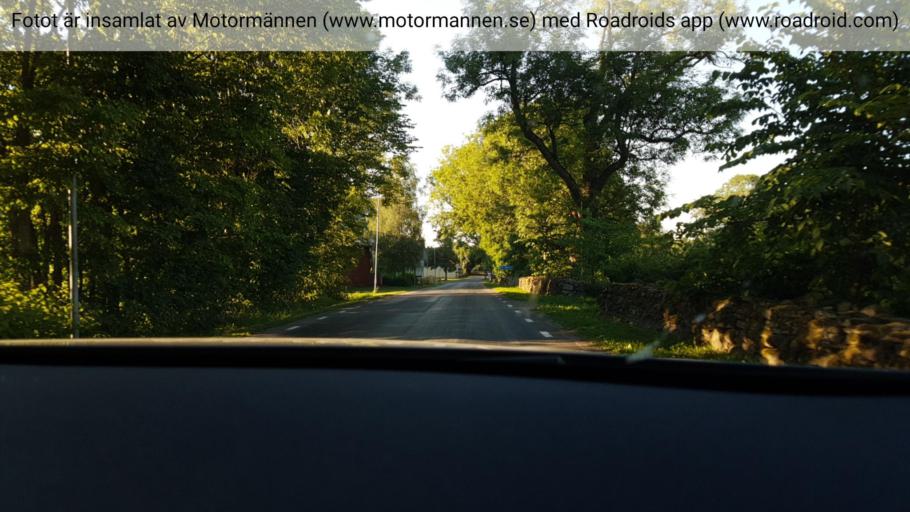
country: SE
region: Vaestra Goetaland
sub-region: Skovde Kommun
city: Skultorp
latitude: 58.2523
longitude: 13.7846
